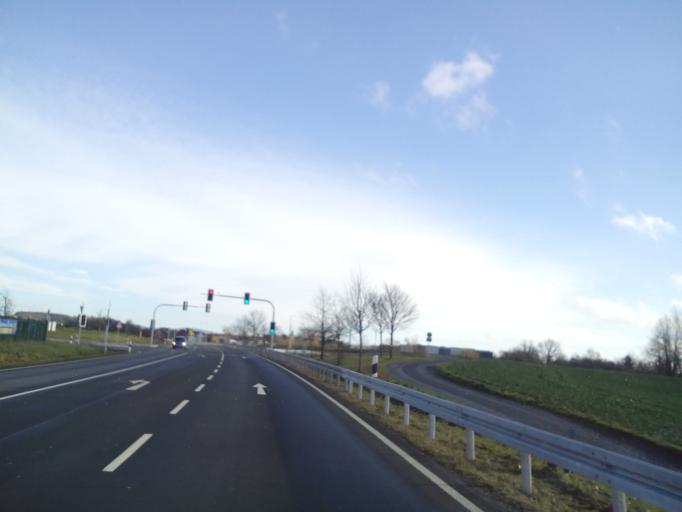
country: DE
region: Bavaria
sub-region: Upper Franconia
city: Mainleus
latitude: 50.1063
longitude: 11.3627
